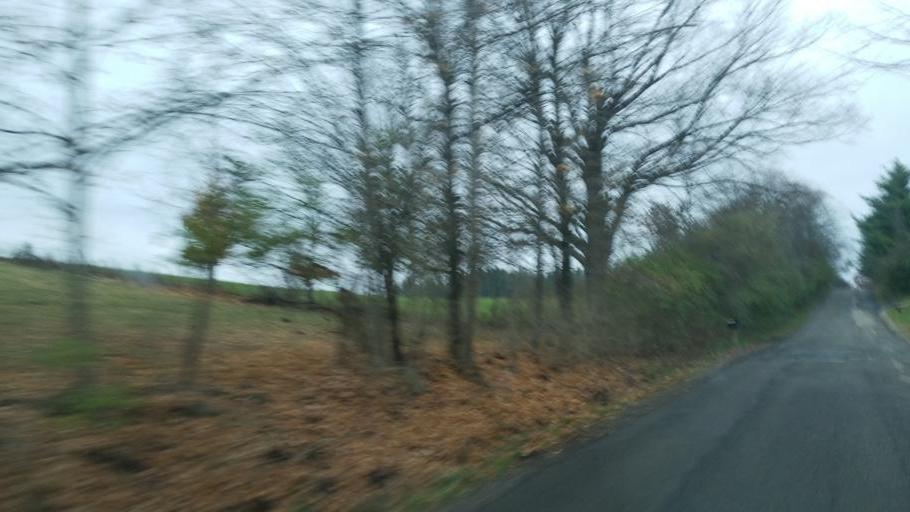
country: US
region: Ohio
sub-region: Knox County
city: Mount Vernon
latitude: 40.3707
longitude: -82.5476
